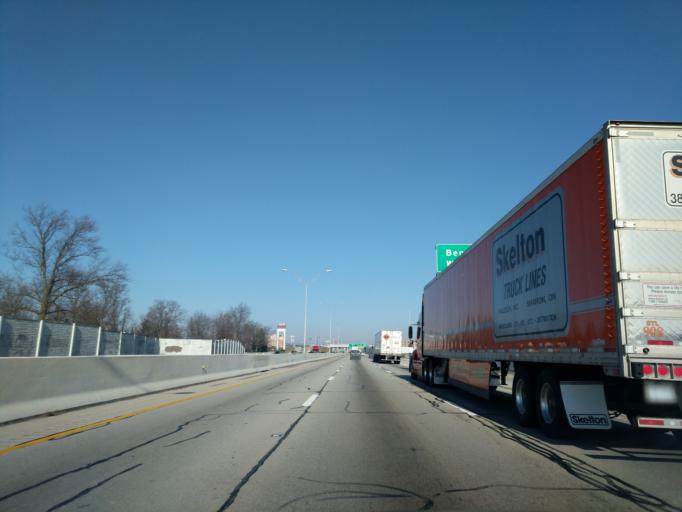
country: US
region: Ohio
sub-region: Montgomery County
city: Northridge
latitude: 39.8357
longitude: -84.1895
